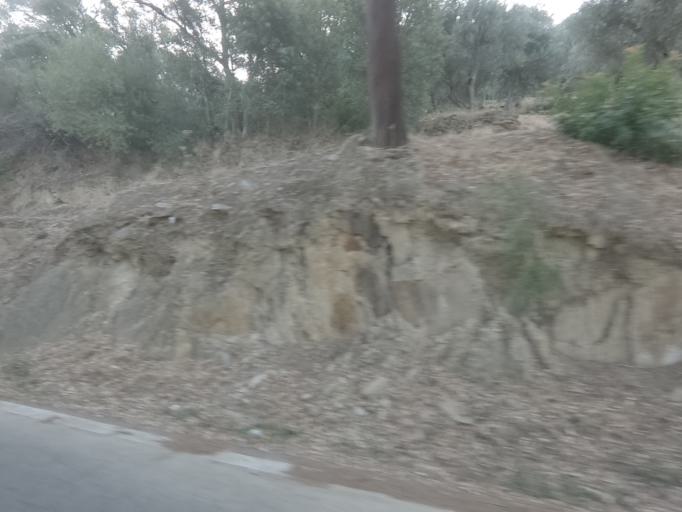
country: PT
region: Vila Real
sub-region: Sabrosa
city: Vilela
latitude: 41.2014
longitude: -7.5372
